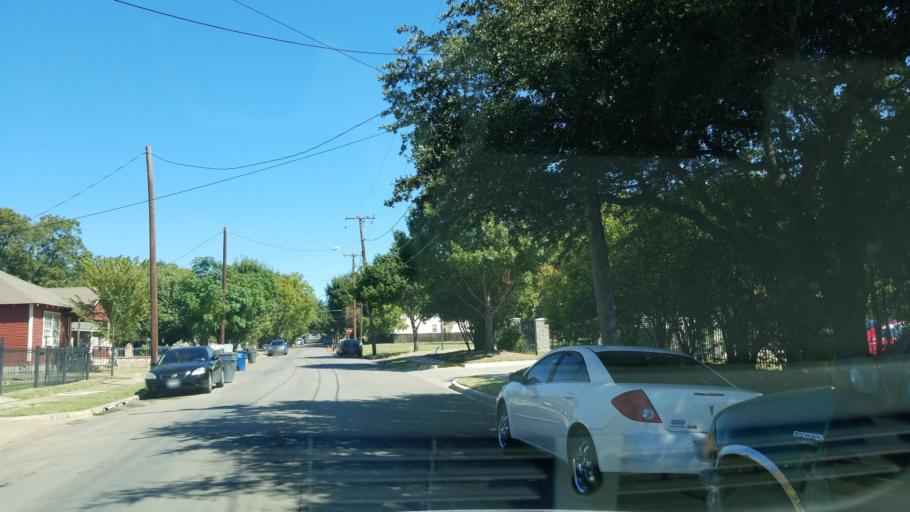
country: US
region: Texas
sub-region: Dallas County
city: Dallas
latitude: 32.7925
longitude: -96.7522
